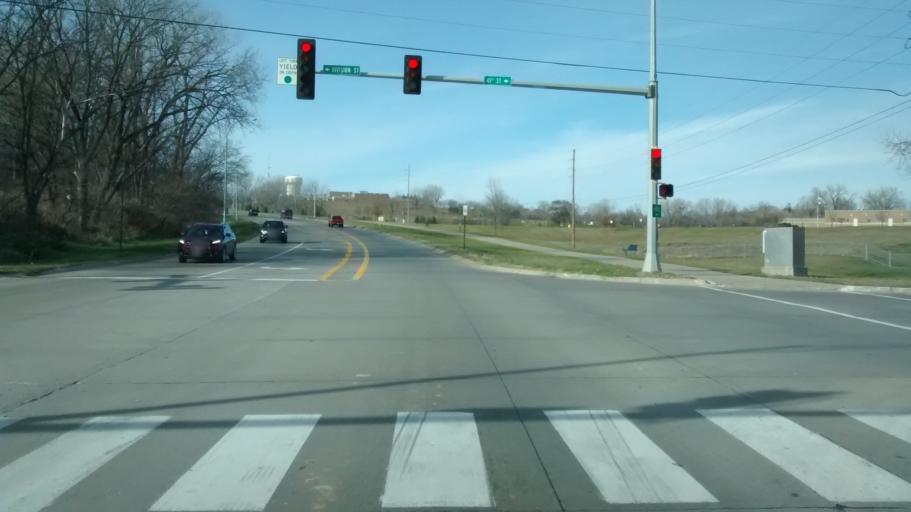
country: US
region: Iowa
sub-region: Woodbury County
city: Sioux City
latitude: 42.5407
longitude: -96.3807
